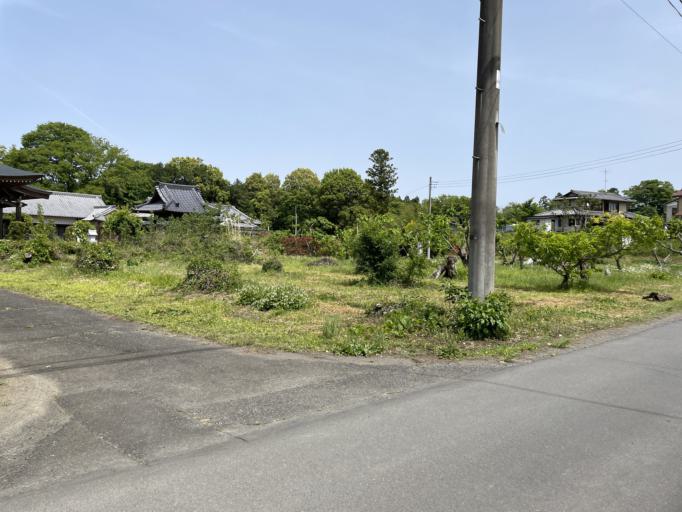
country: JP
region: Saitama
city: Hanno
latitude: 35.8907
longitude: 139.3186
